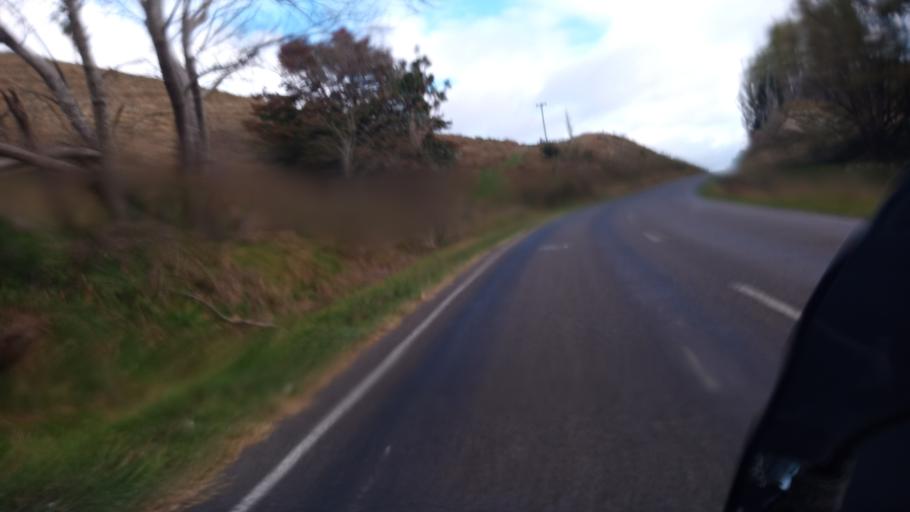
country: NZ
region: Gisborne
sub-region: Gisborne District
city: Gisborne
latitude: -38.5887
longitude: 177.7644
